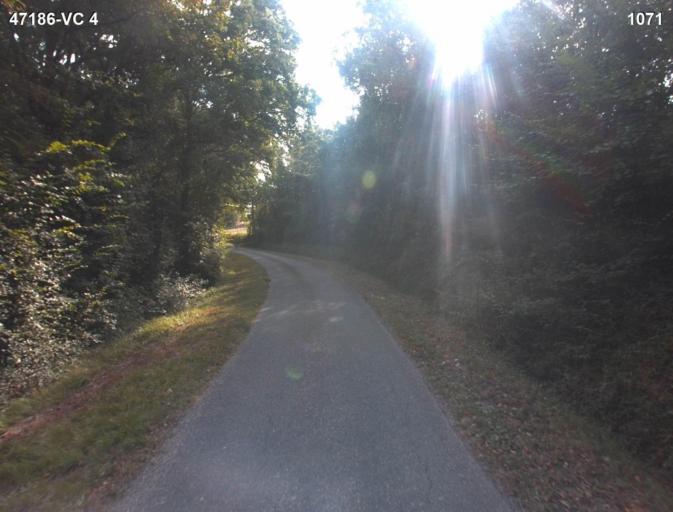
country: FR
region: Aquitaine
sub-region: Departement du Lot-et-Garonne
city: Port-Sainte-Marie
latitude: 44.2013
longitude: 0.4290
